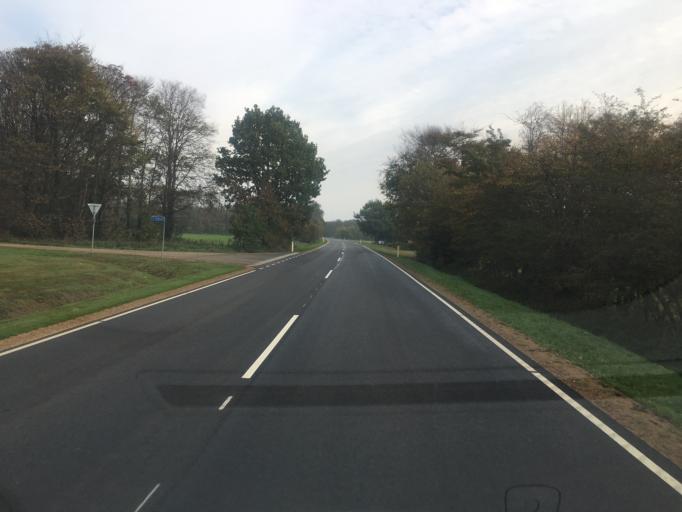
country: DK
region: South Denmark
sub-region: Tonder Kommune
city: Logumkloster
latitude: 55.0931
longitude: 9.0187
